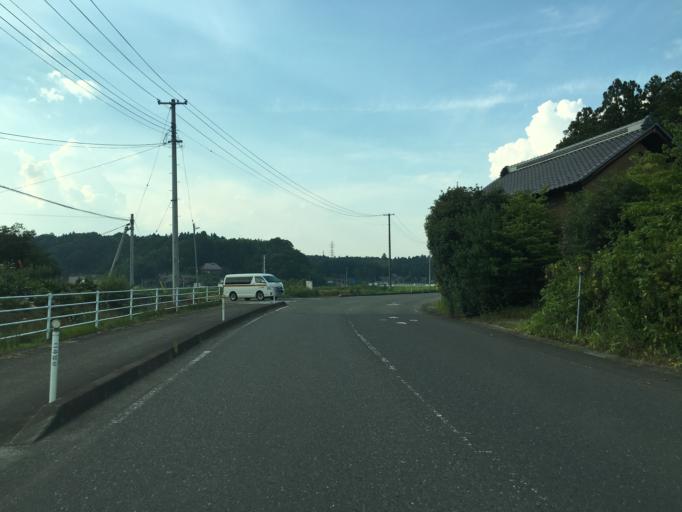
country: JP
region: Fukushima
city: Nihommatsu
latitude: 37.5610
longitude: 140.4354
